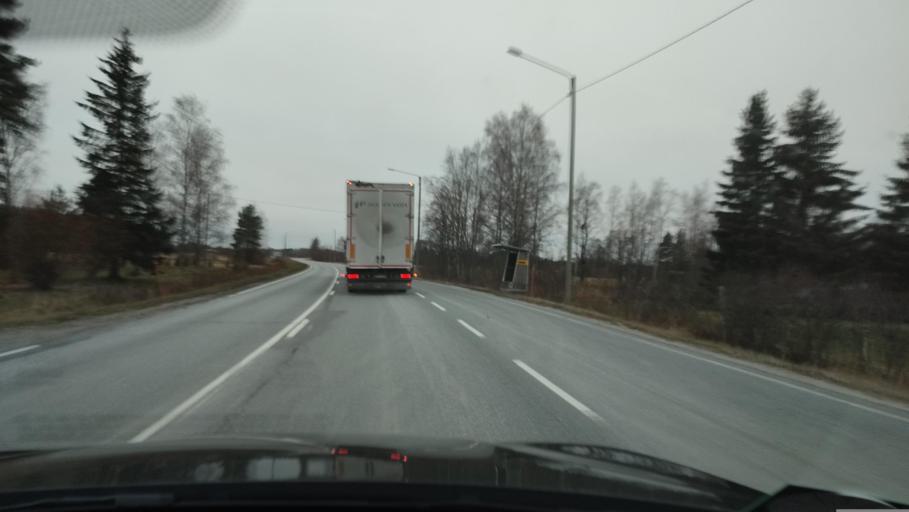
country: FI
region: Southern Ostrobothnia
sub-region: Suupohja
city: Kauhajoki
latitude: 62.3553
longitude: 22.0601
